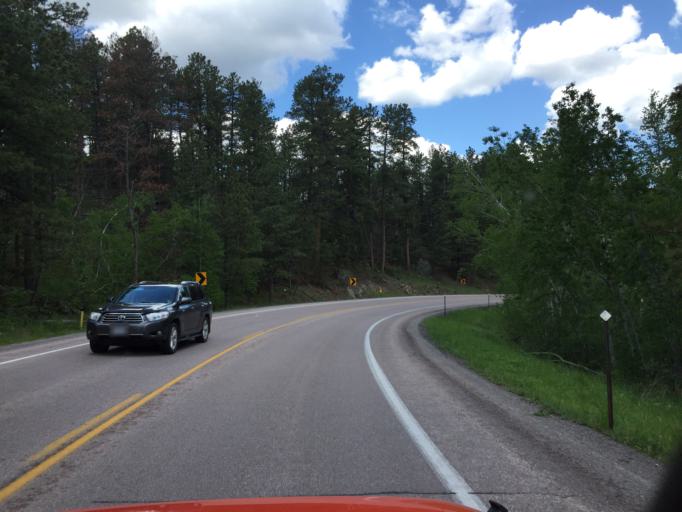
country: US
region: South Dakota
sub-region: Custer County
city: Custer
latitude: 43.8882
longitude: -103.4783
